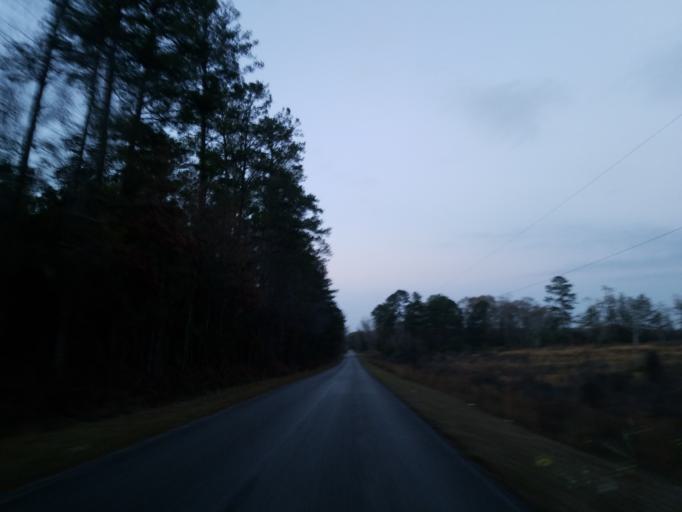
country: US
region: Alabama
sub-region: Sumter County
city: York
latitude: 32.4183
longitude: -88.4383
